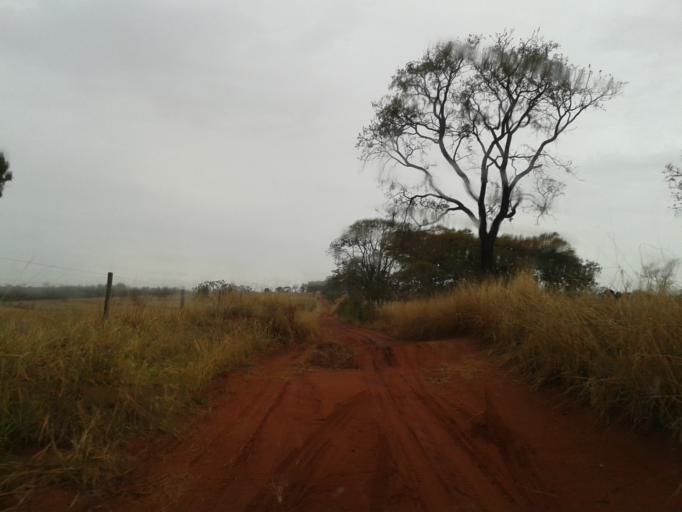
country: BR
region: Minas Gerais
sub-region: Campina Verde
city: Campina Verde
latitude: -19.3529
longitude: -49.5467
